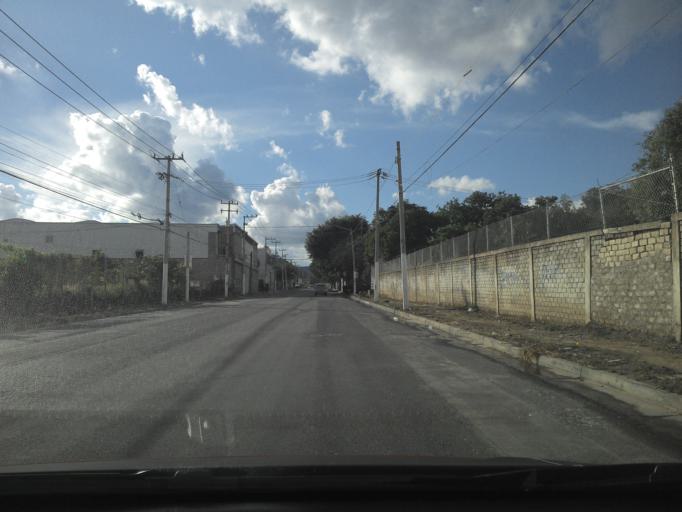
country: MX
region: Jalisco
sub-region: Tlajomulco de Zuniga
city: Palomar
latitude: 20.6163
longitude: -103.4447
